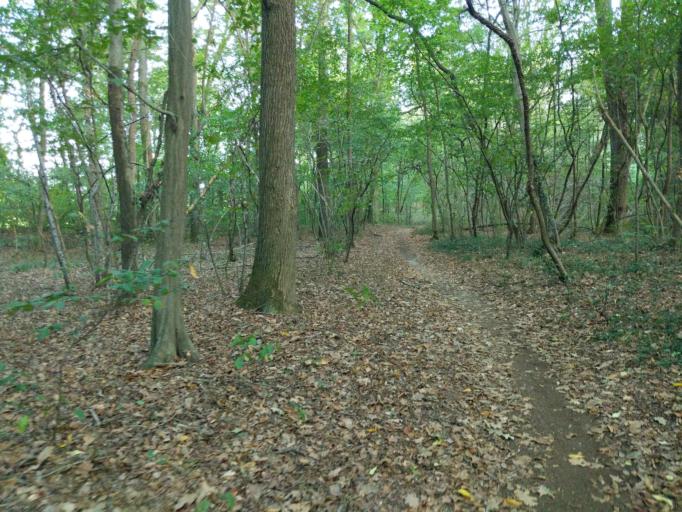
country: IT
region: Lombardy
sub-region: Citta metropolitana di Milano
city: Turbigo
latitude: 45.5248
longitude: 8.7226
